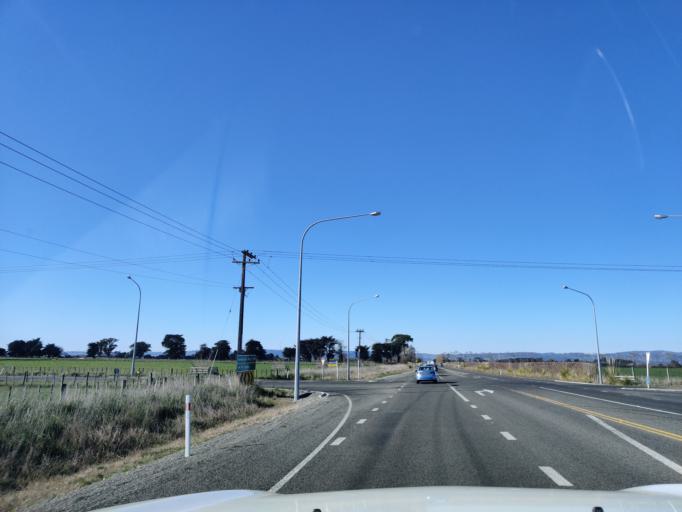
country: NZ
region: Manawatu-Wanganui
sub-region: Palmerston North City
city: Palmerston North
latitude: -40.2953
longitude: 175.5731
